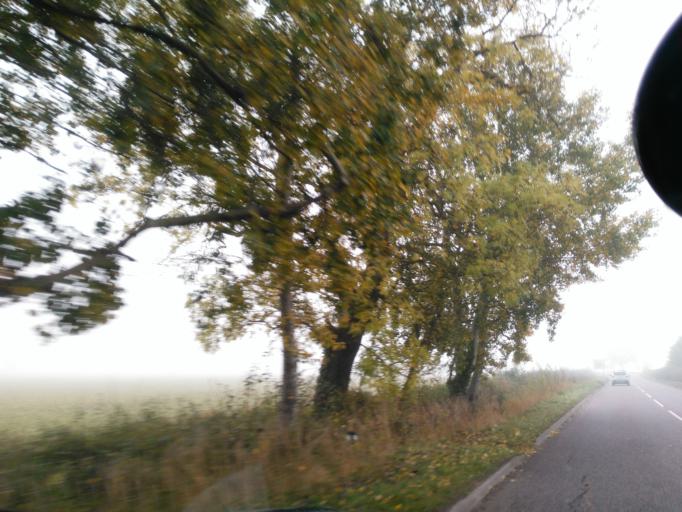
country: GB
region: England
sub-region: Wiltshire
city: Seend
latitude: 51.3545
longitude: -2.0643
